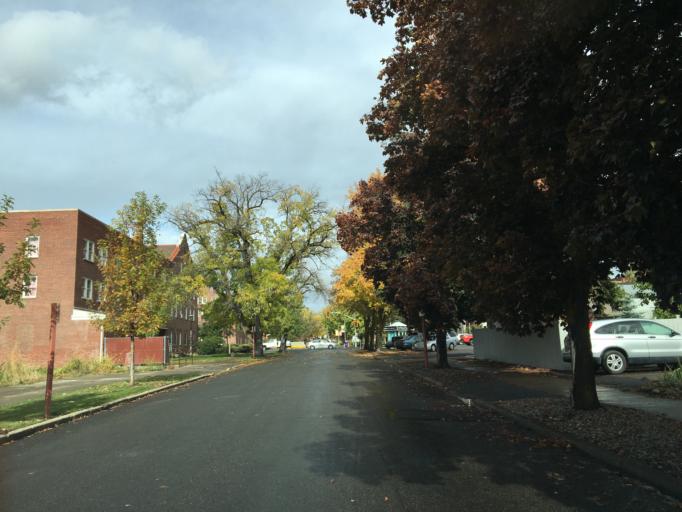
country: US
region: Washington
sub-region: Kittitas County
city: Ellensburg
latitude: 46.9990
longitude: -120.5393
